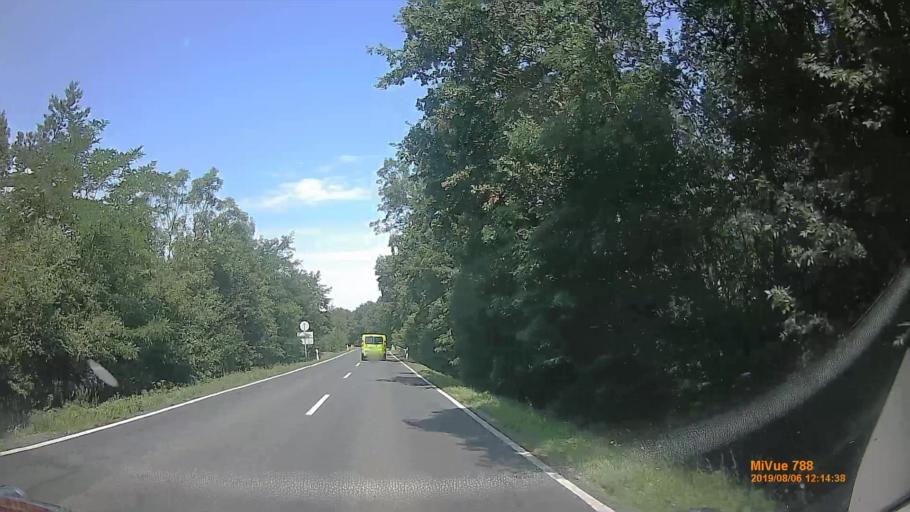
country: HU
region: Vas
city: Vasvar
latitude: 47.1414
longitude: 16.8282
